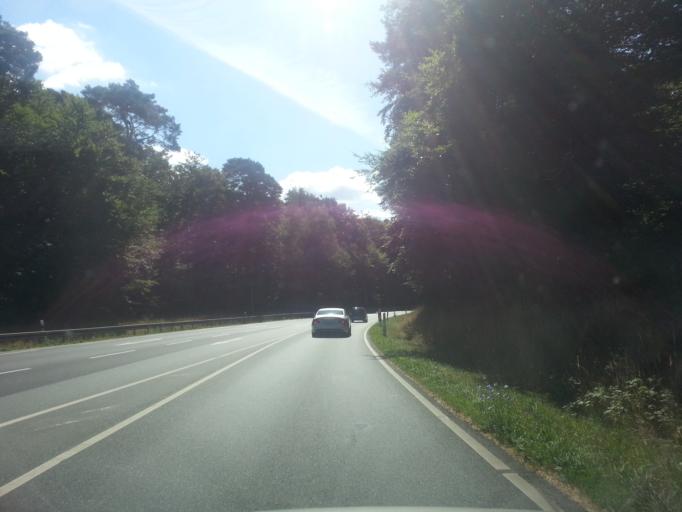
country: DE
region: Hesse
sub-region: Regierungsbezirk Darmstadt
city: Dietzenbach
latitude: 50.0125
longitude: 8.8059
